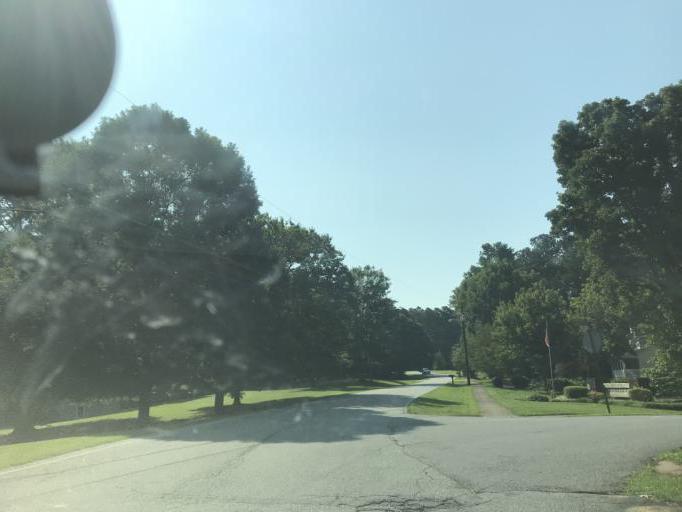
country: US
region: Georgia
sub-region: Forsyth County
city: Cumming
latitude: 34.2313
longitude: -84.1225
